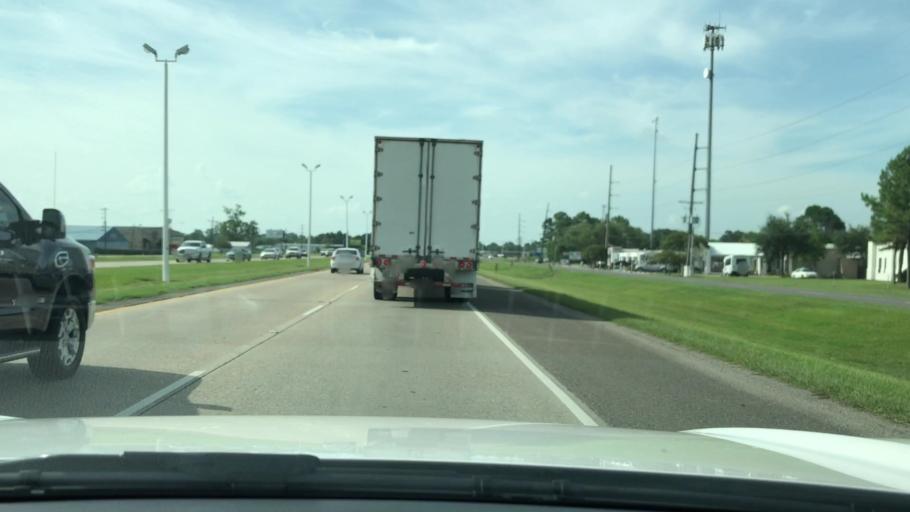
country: US
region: Louisiana
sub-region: West Baton Rouge Parish
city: Addis
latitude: 30.3579
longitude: -91.2600
